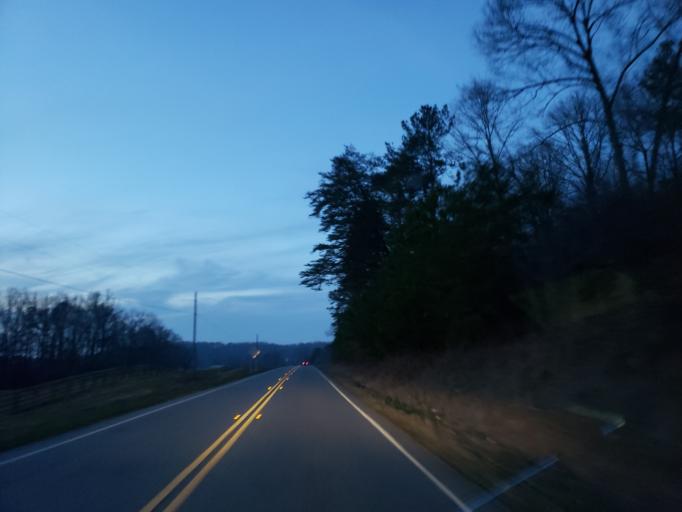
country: US
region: Georgia
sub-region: Cherokee County
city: Ball Ground
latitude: 34.2918
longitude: -84.2736
